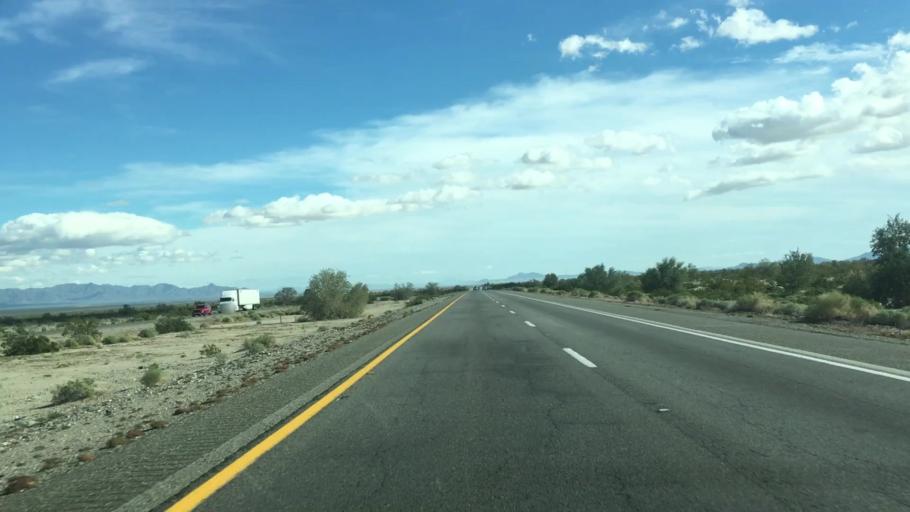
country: US
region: California
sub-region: Riverside County
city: Mesa Verde
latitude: 33.6674
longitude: -115.1930
